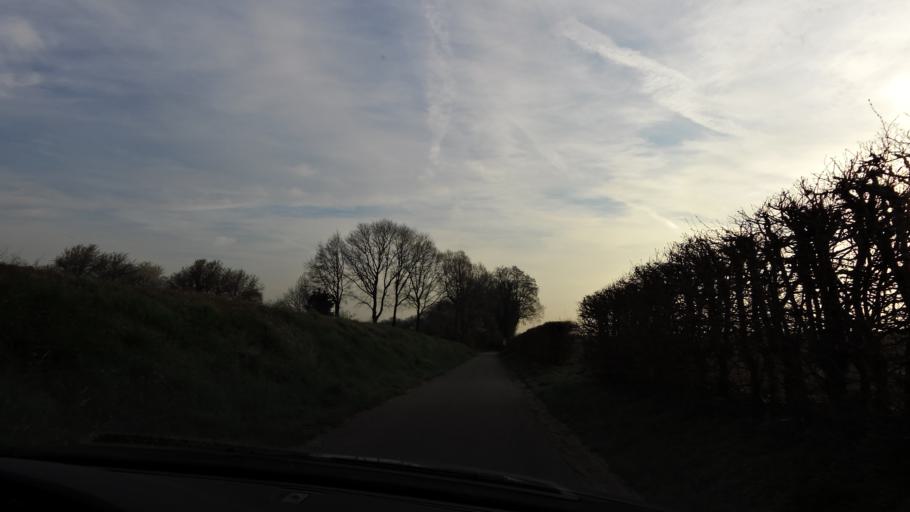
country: NL
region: Limburg
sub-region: Gemeente Onderbanken
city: Merkelbeek
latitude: 50.9689
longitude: 5.9468
